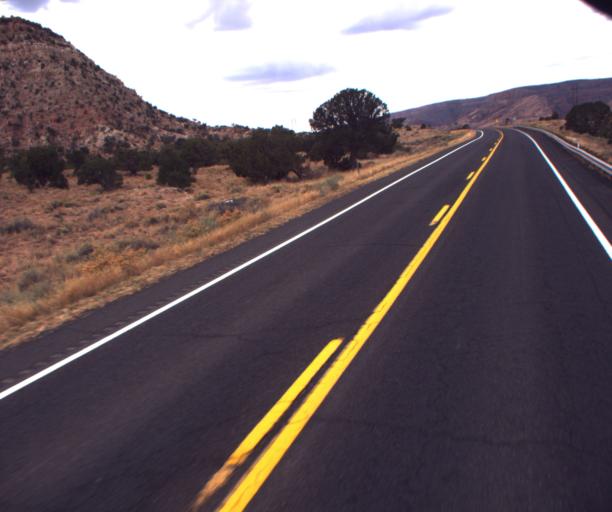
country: US
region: Arizona
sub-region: Navajo County
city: Kayenta
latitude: 36.6942
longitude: -110.3601
